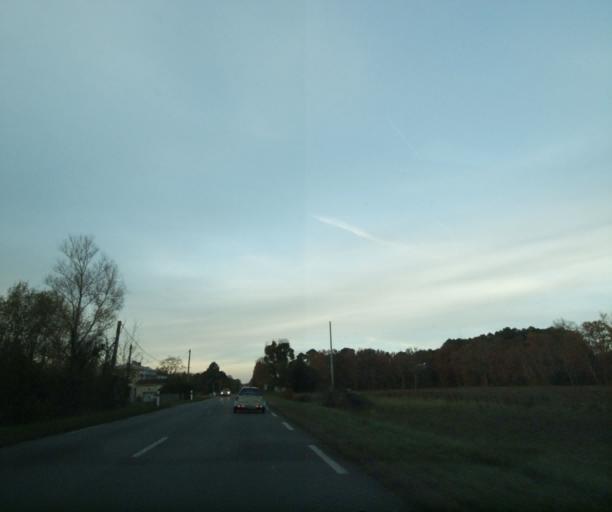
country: FR
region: Aquitaine
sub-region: Departement de la Gironde
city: Bazas
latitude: 44.4853
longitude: -0.2319
